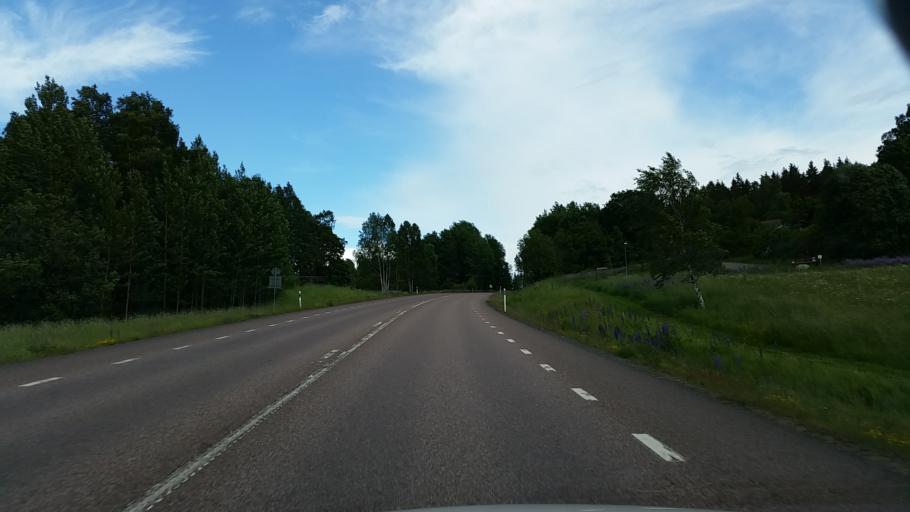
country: SE
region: Dalarna
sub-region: Smedjebackens Kommun
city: Smedjebacken
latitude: 60.1385
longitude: 15.3878
